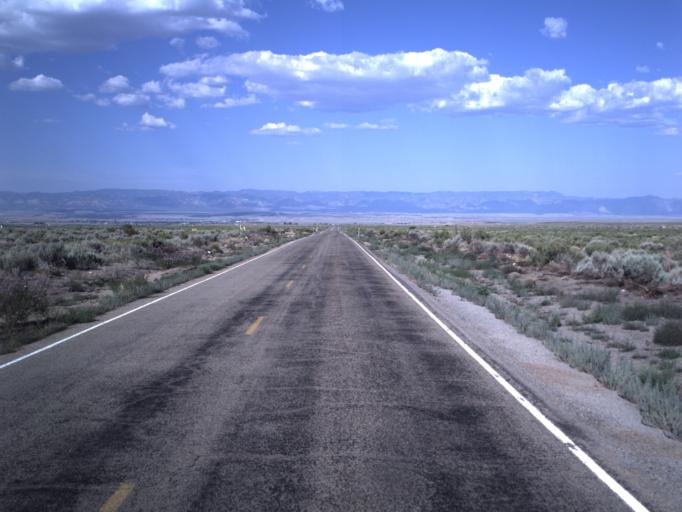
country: US
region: Utah
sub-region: Carbon County
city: Price
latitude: 39.4866
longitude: -110.8773
